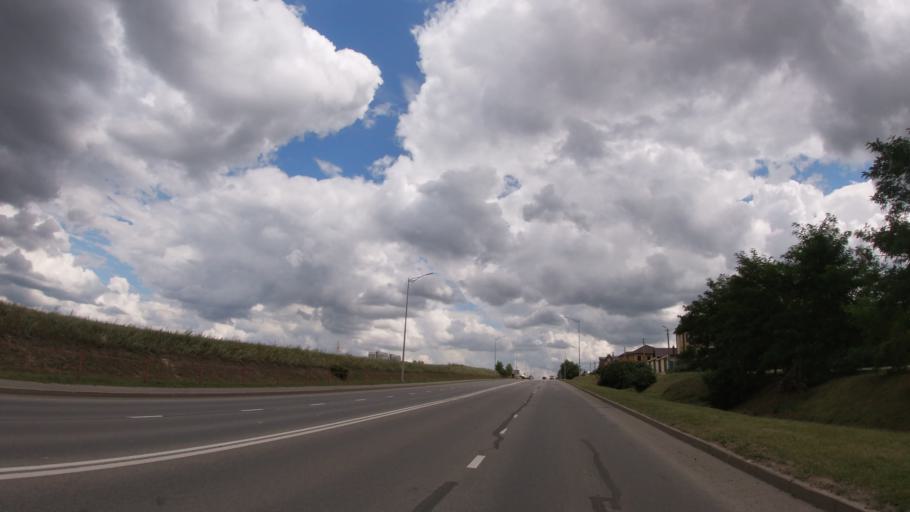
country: RU
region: Belgorod
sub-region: Belgorodskiy Rayon
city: Belgorod
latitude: 50.5508
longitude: 36.5542
